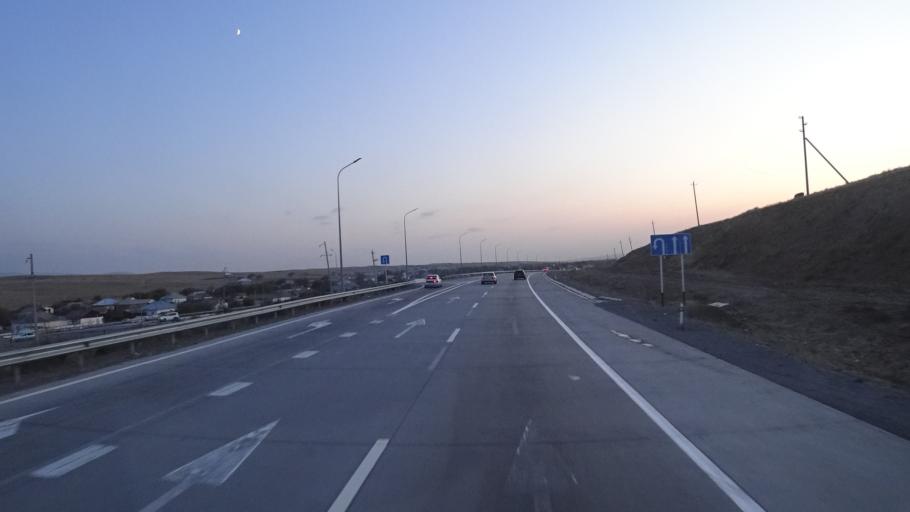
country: KZ
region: Ongtustik Qazaqstan
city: Qazyqurt
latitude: 41.8978
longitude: 69.4538
